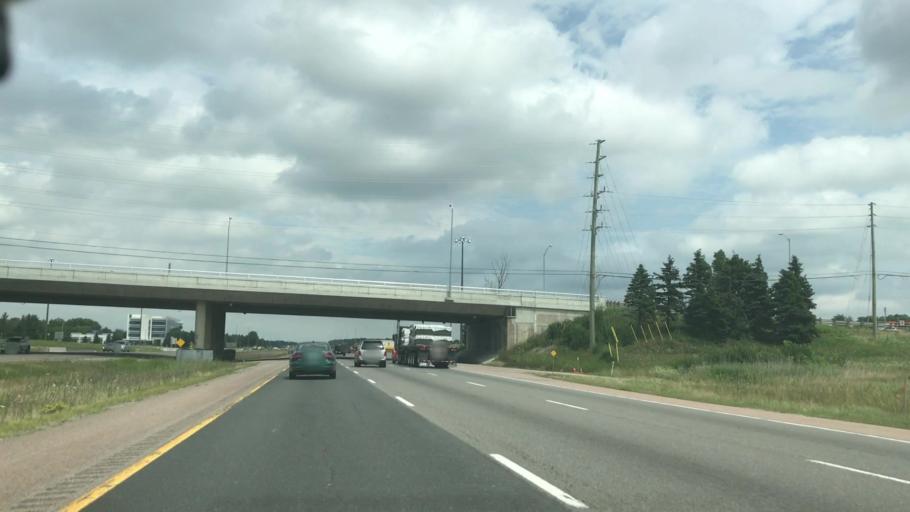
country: CA
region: Ontario
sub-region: York
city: Richmond Hill
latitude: 43.8823
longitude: -79.3794
